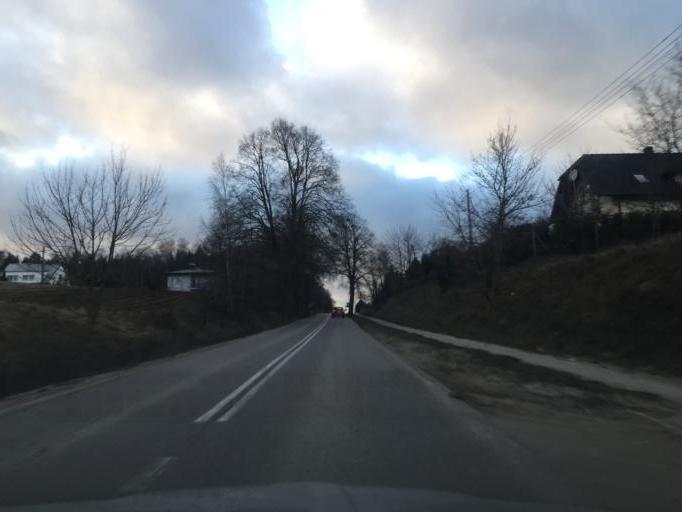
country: PL
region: Pomeranian Voivodeship
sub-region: Powiat kartuski
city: Banino
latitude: 54.3879
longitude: 18.4203
